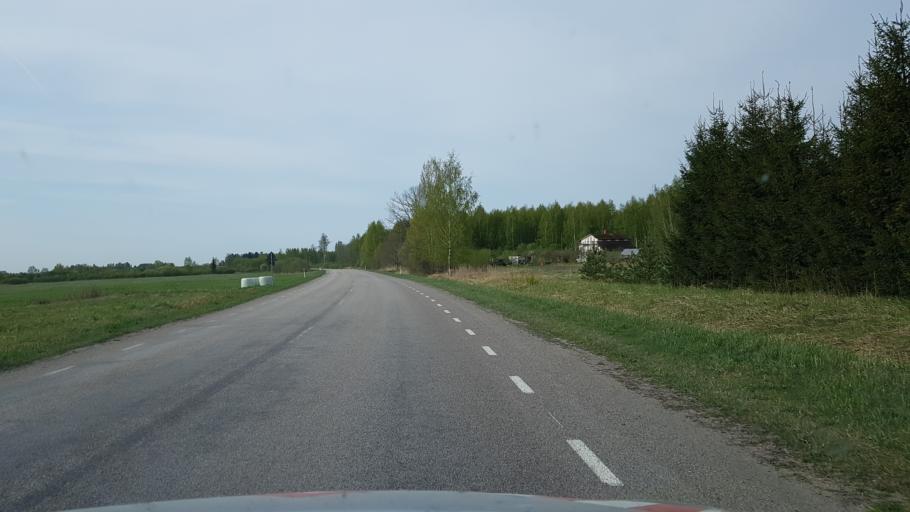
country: EE
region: Paernumaa
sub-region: Audru vald
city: Audru
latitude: 58.3911
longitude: 24.2767
